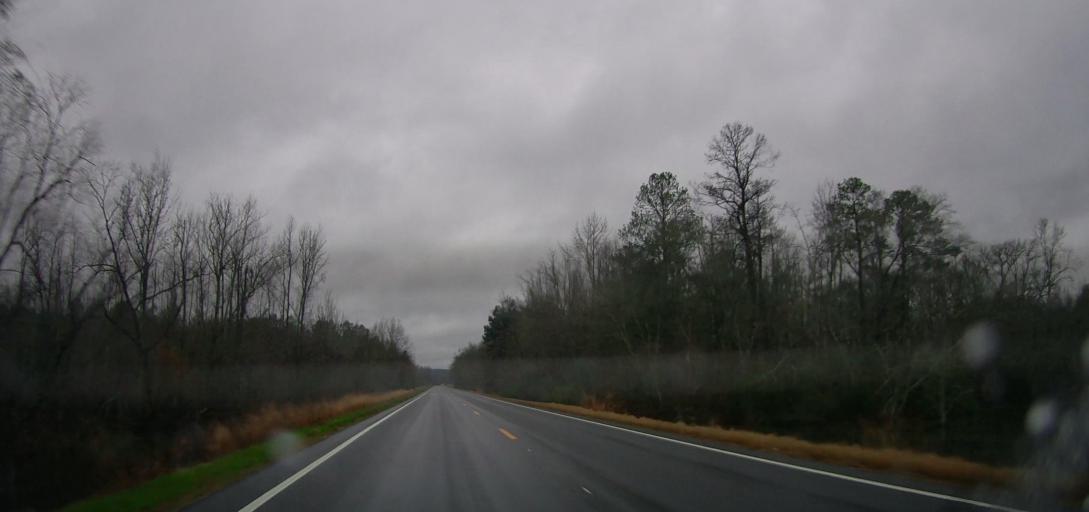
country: US
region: Alabama
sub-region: Chilton County
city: Thorsby
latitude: 32.7618
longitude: -86.8751
